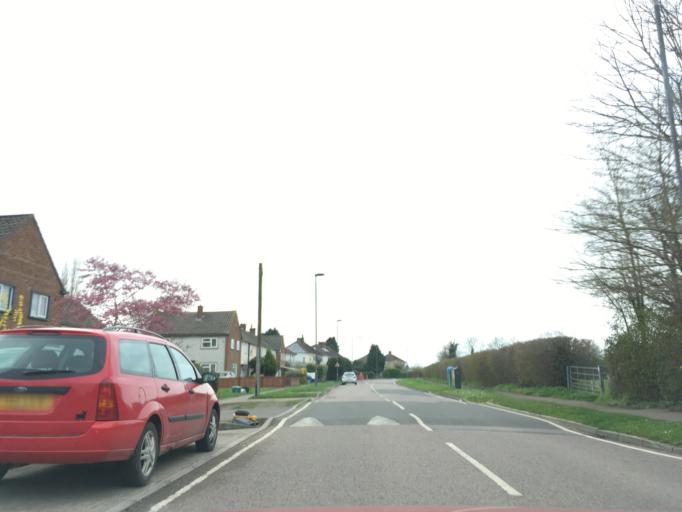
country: GB
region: England
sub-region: South Gloucestershire
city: Stoke Gifford
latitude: 51.5259
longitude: -2.5551
